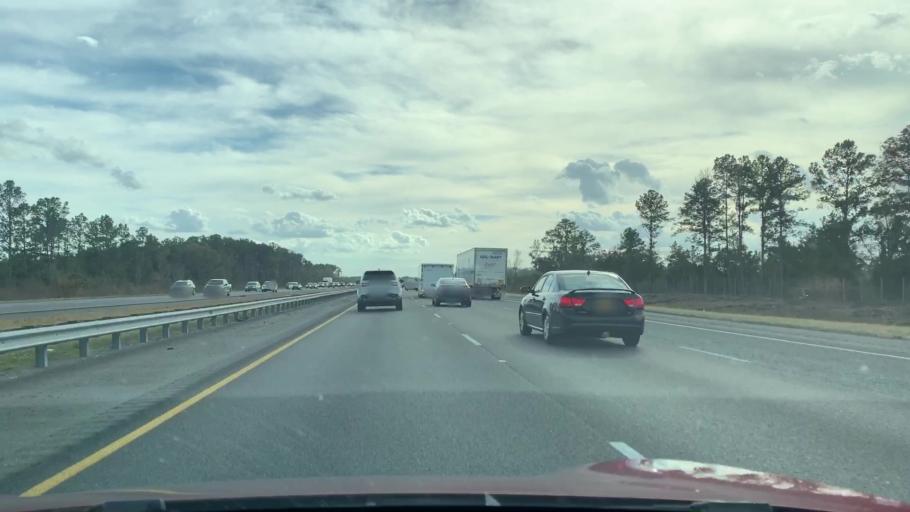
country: US
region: Georgia
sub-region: Camden County
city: Woodbine
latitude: 31.0057
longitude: -81.6625
